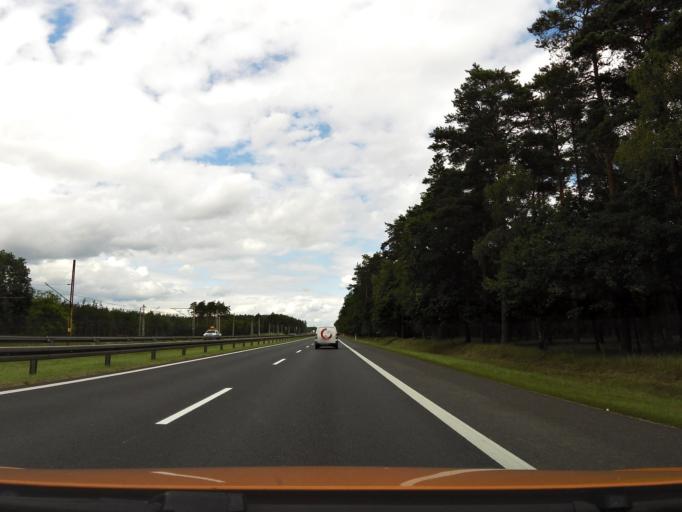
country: PL
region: West Pomeranian Voivodeship
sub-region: Powiat goleniowski
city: Goleniow
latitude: 53.4967
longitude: 14.7976
